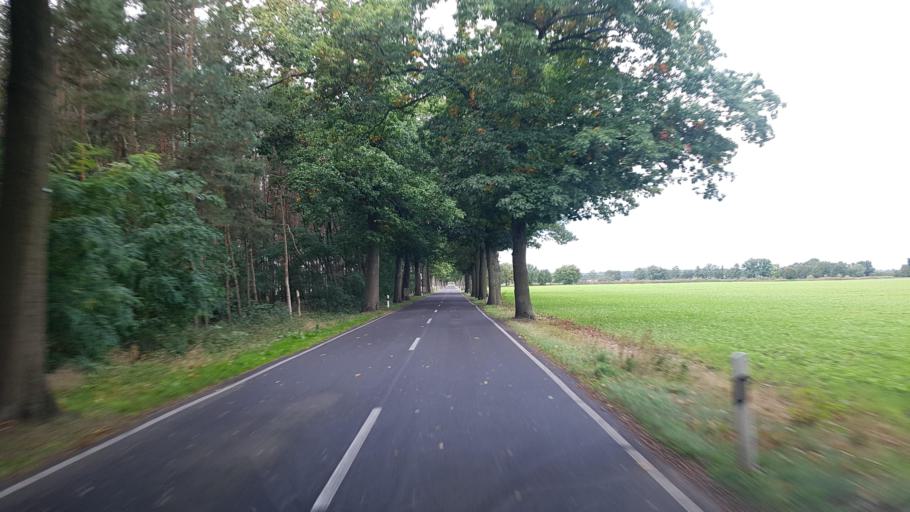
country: DE
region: Brandenburg
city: Kasel-Golzig
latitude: 51.9350
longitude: 13.6742
